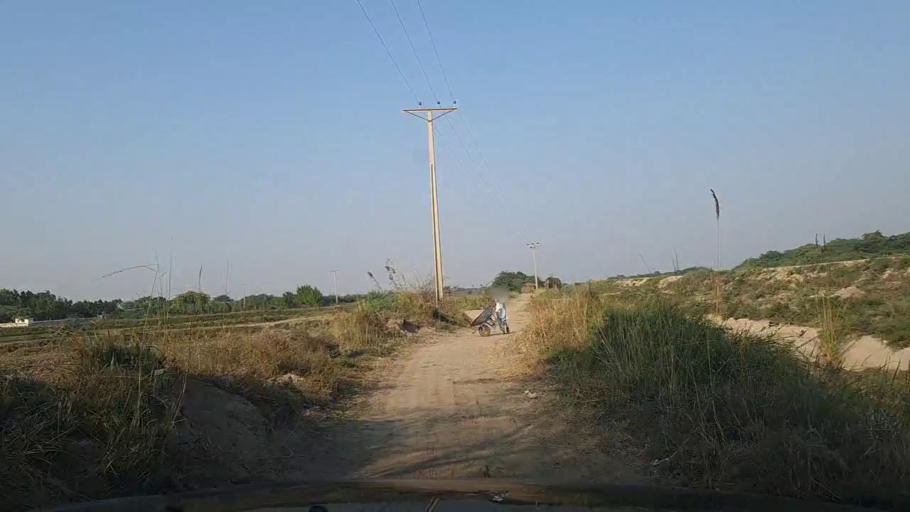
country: PK
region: Sindh
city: Thatta
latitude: 24.7573
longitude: 67.9605
